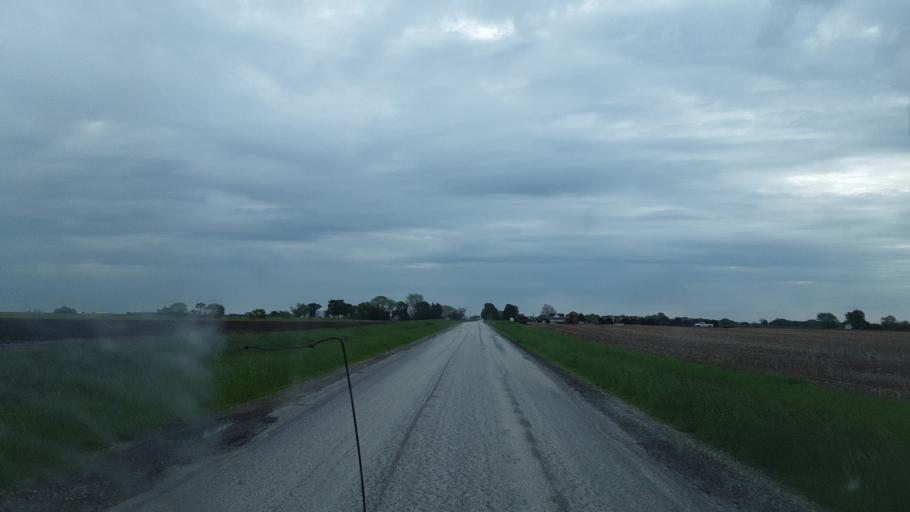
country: US
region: Illinois
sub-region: McDonough County
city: Macomb
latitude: 40.3819
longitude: -90.6652
